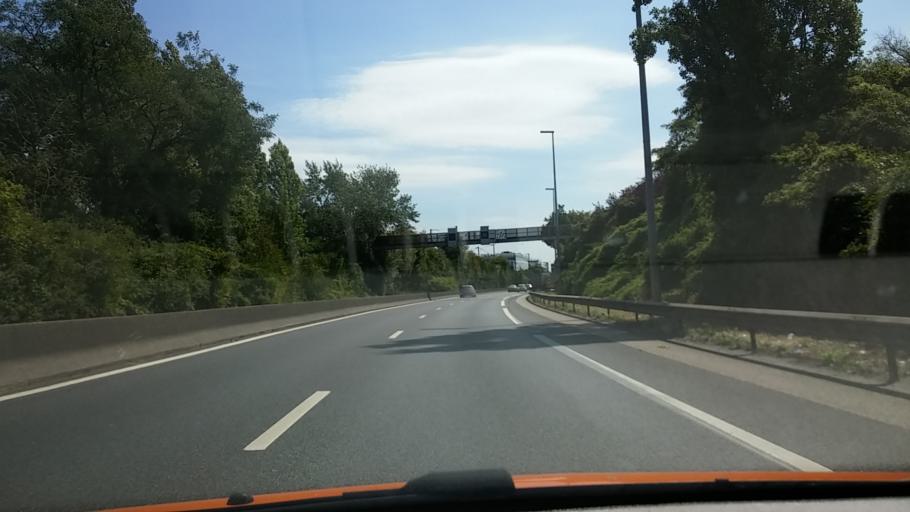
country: FR
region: Ile-de-France
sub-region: Departement du Val-de-Marne
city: Fontenay-sous-Bois
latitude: 48.8590
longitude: 2.4865
